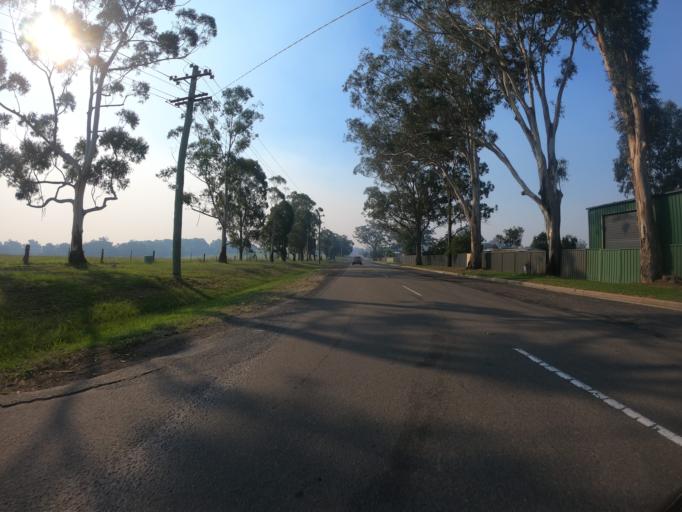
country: AU
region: New South Wales
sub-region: Wollondilly
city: Douglas Park
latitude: -34.2069
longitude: 150.7847
